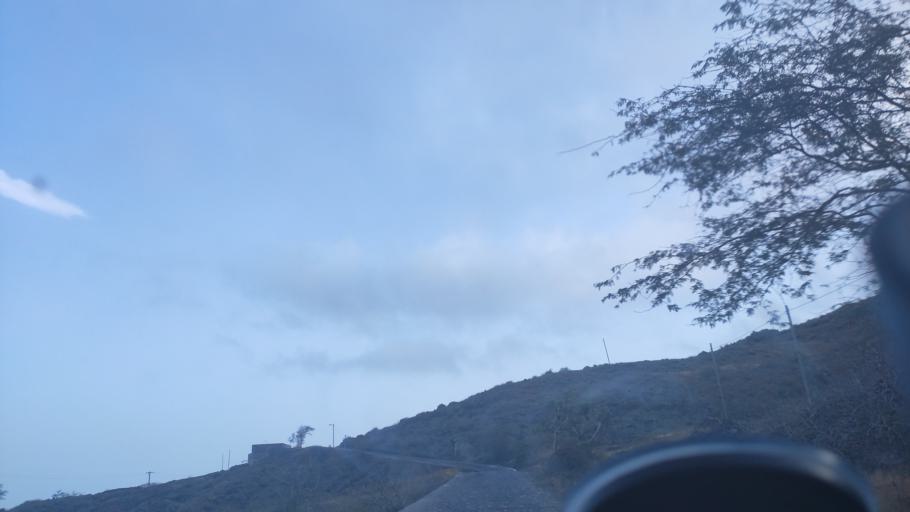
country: CV
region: Mosteiros
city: Porto dos Mosteiros
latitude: 15.0071
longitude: -24.3053
